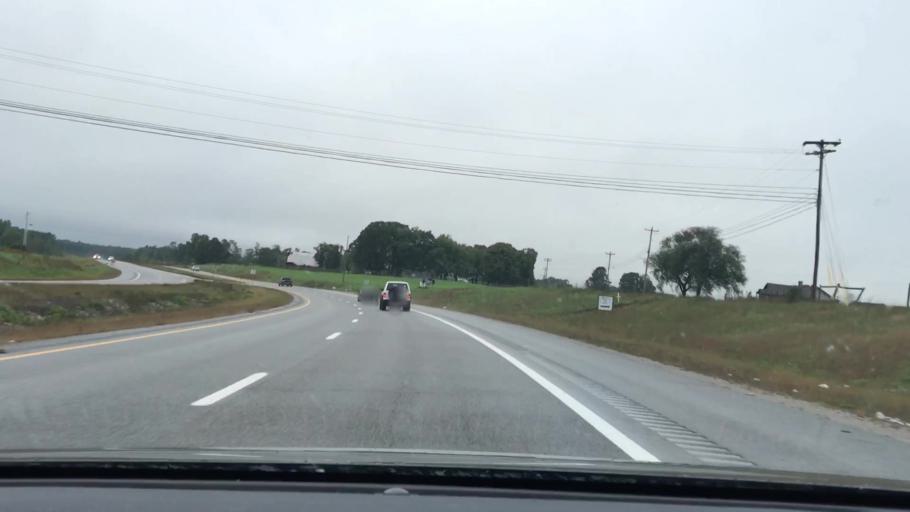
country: US
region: Tennessee
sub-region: Fentress County
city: Grimsley
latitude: 36.3189
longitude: -84.9651
